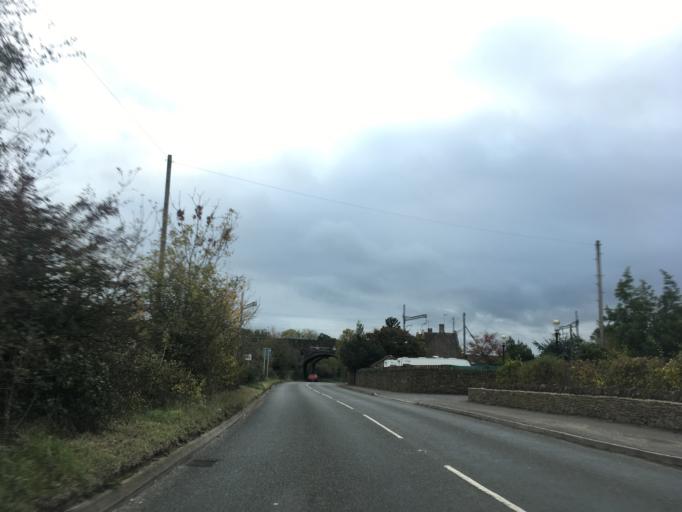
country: GB
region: England
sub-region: South Gloucestershire
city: Yate
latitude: 51.5223
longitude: -2.4346
